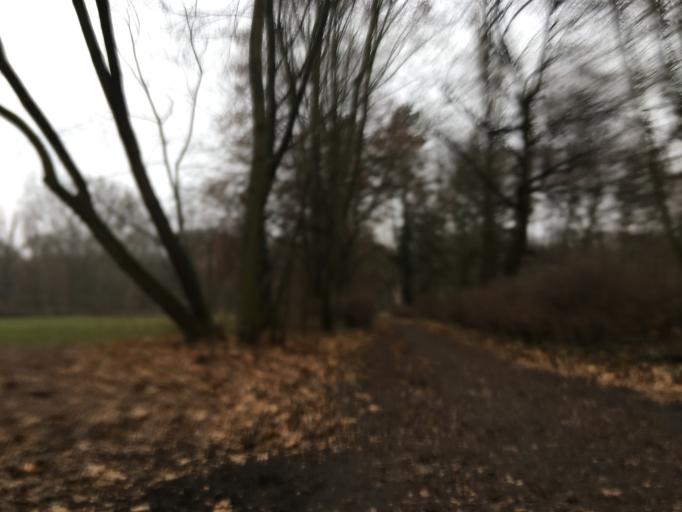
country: DE
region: Berlin
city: Pankow
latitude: 52.5750
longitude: 13.3849
